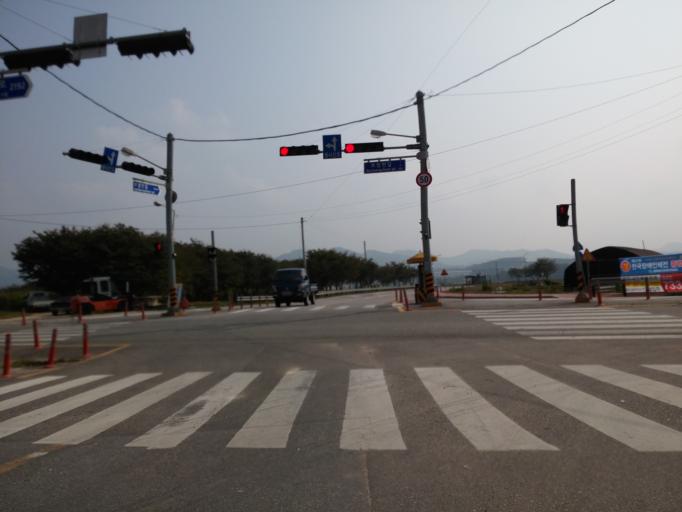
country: KR
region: Chungcheongbuk-do
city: Yong-dong
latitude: 36.3440
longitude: 127.7928
